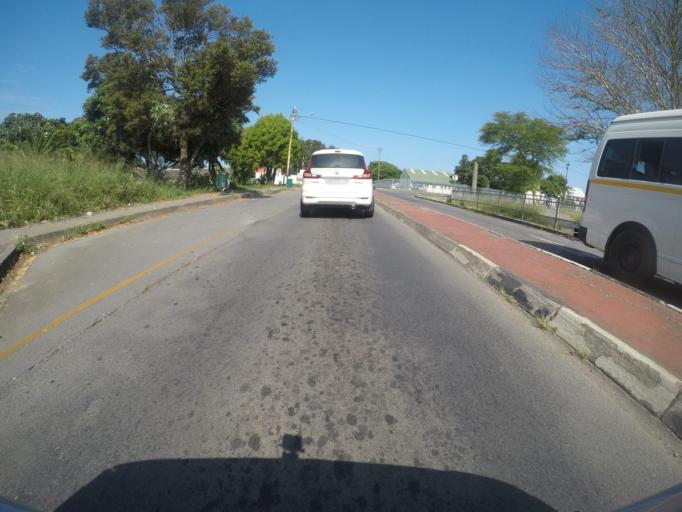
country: ZA
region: Eastern Cape
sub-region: Buffalo City Metropolitan Municipality
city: East London
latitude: -32.9736
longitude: 27.8864
